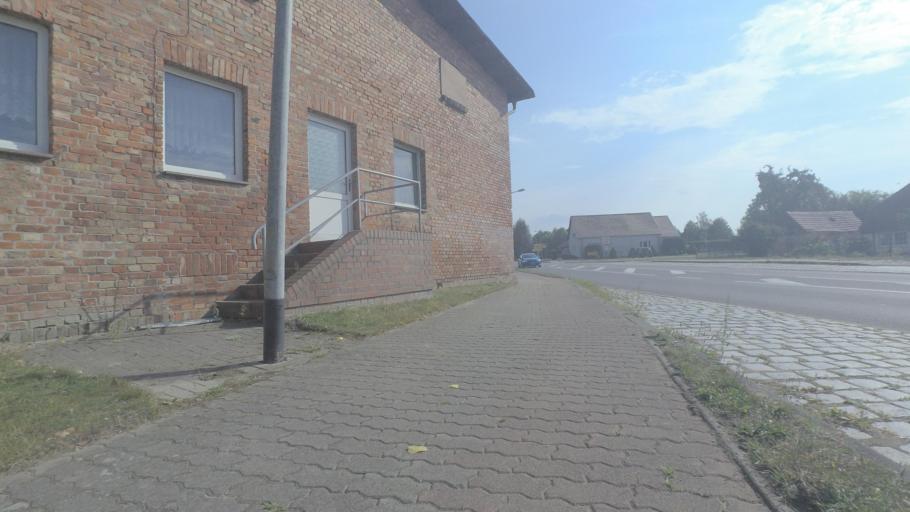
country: DE
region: Mecklenburg-Vorpommern
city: Grimmen
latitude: 54.0553
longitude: 13.1191
